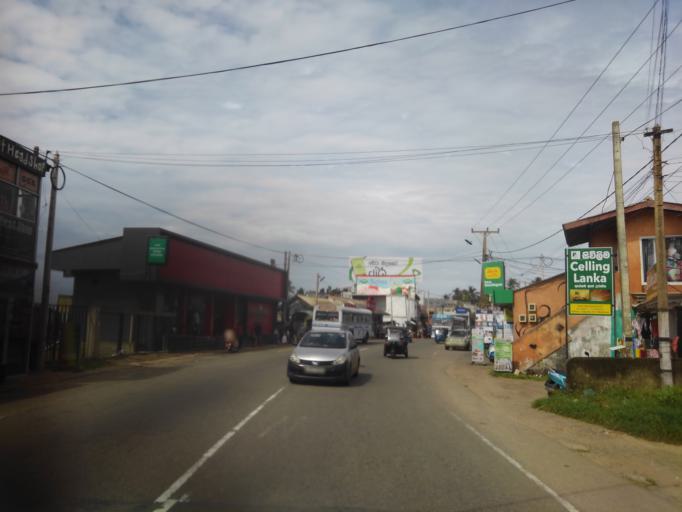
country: LK
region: Southern
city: Hikkaduwa
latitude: 6.1391
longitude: 80.0997
